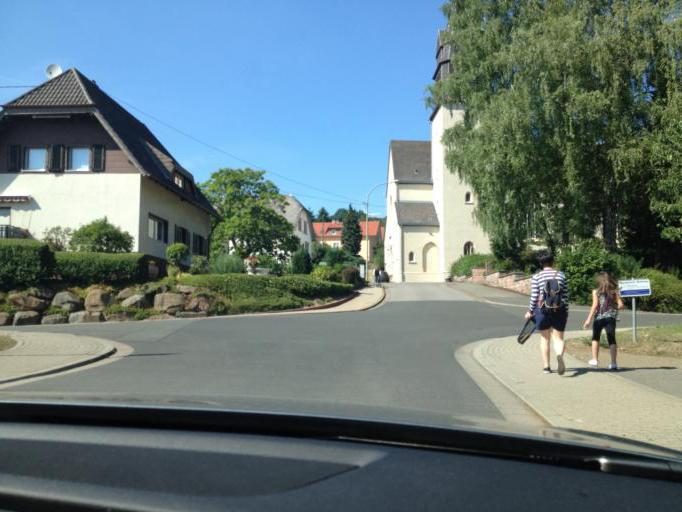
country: DE
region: Saarland
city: Oberthal
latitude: 49.5143
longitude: 7.0865
